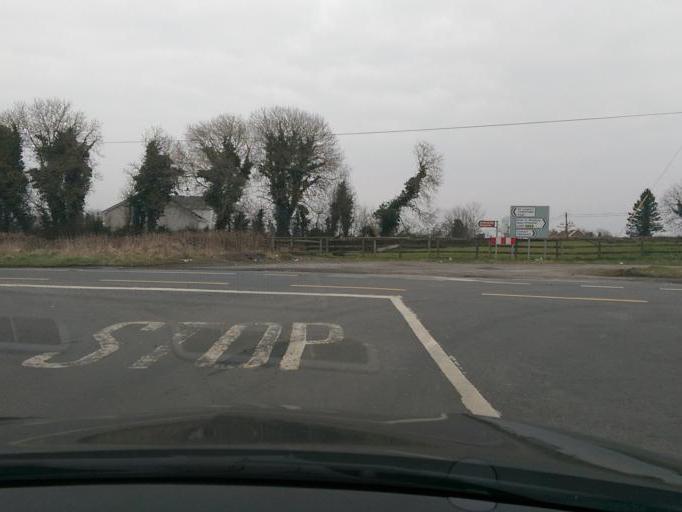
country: IE
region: Leinster
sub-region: An Longfort
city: Longford
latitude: 53.6592
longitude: -7.8215
